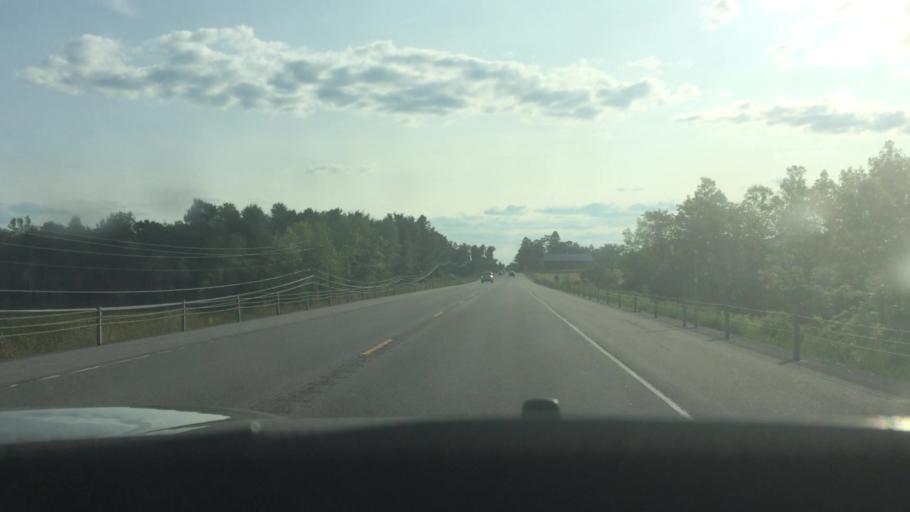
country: US
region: New York
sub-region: St. Lawrence County
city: Potsdam
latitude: 44.6407
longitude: -75.0662
